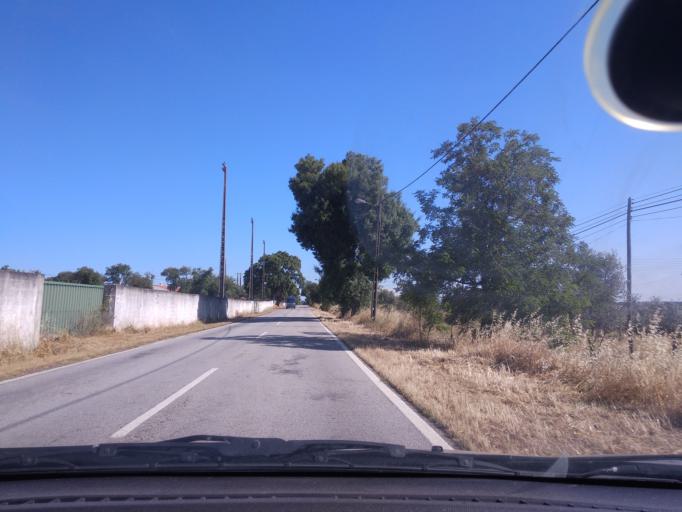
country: PT
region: Portalegre
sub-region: Nisa
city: Nisa
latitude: 39.4251
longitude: -7.6208
